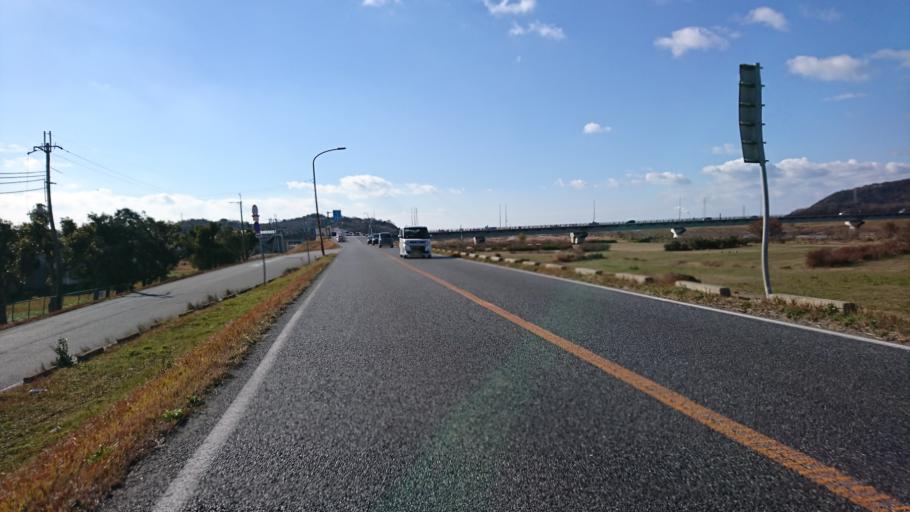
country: JP
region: Hyogo
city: Kakogawacho-honmachi
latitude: 34.7900
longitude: 134.8697
